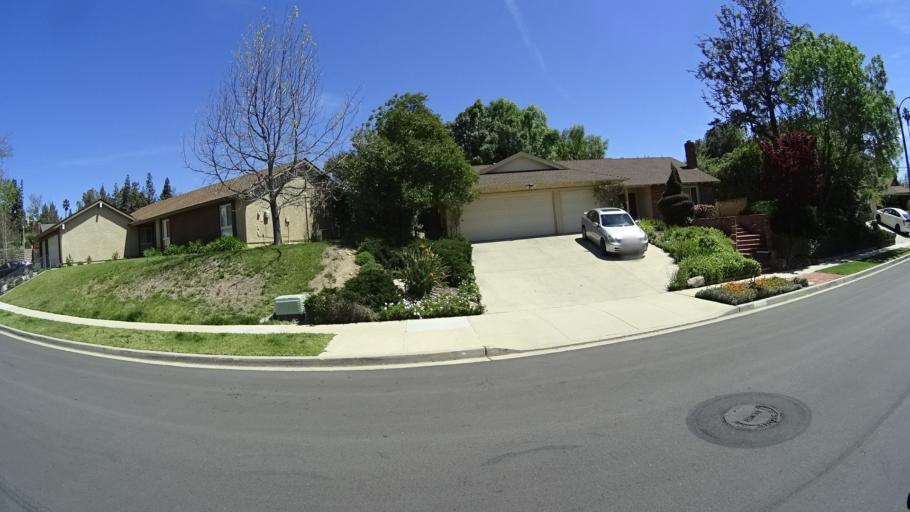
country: US
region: California
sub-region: Ventura County
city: Thousand Oaks
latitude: 34.2183
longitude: -118.8552
